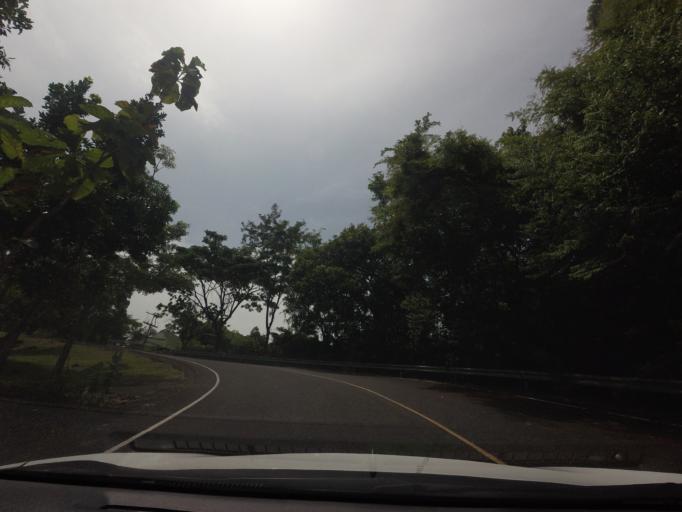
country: TH
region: Chon Buri
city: Ban Bueng
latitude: 13.2125
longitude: 101.0707
